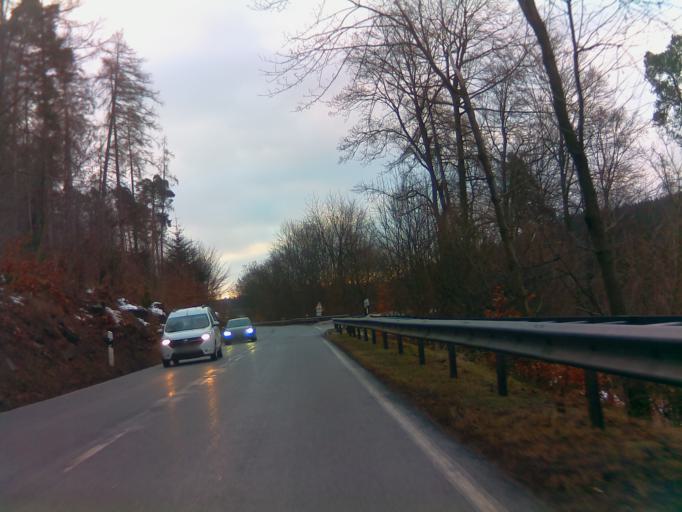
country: DE
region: Baden-Wuerttemberg
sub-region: Karlsruhe Region
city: Zwingenberg
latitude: 49.4528
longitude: 9.0295
